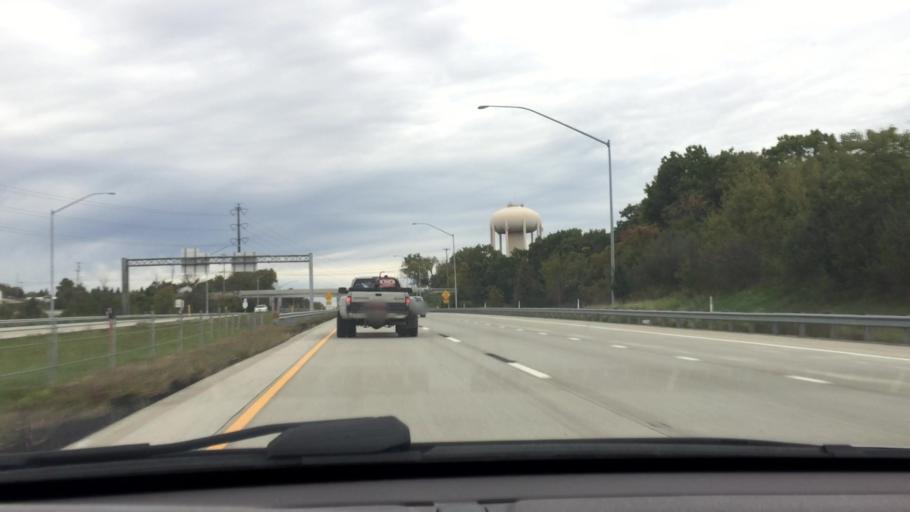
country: US
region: Pennsylvania
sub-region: Allegheny County
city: Carnot-Moon
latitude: 40.5296
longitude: -80.2723
